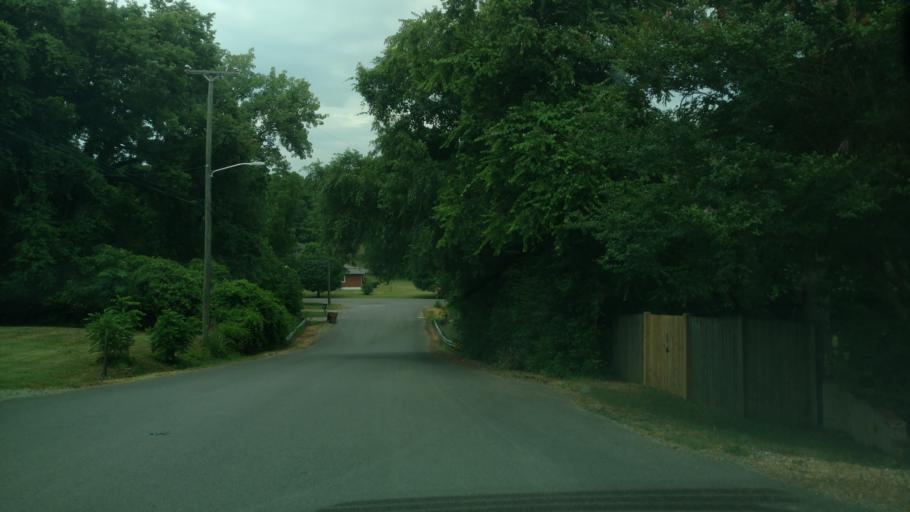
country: US
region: Tennessee
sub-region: Davidson County
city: Nashville
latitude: 36.2055
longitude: -86.7119
